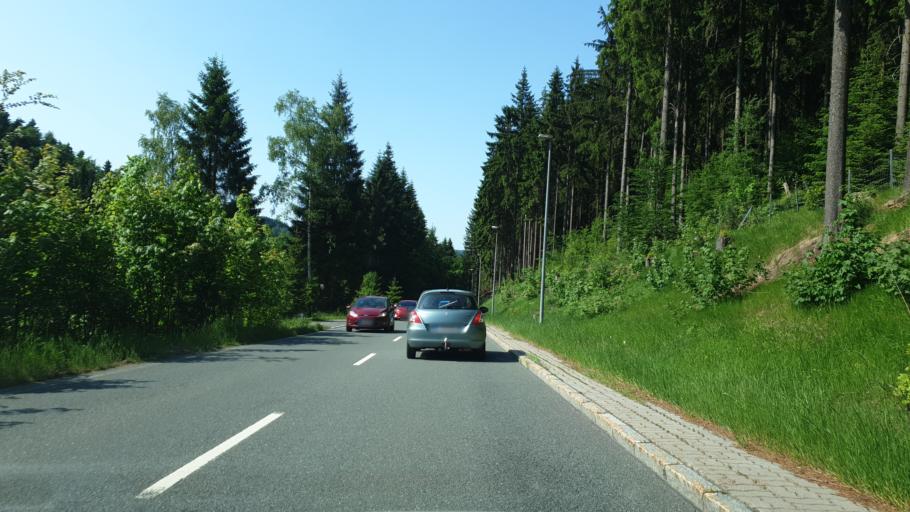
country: DE
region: Saxony
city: Klingenthal
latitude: 50.3889
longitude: 12.4927
